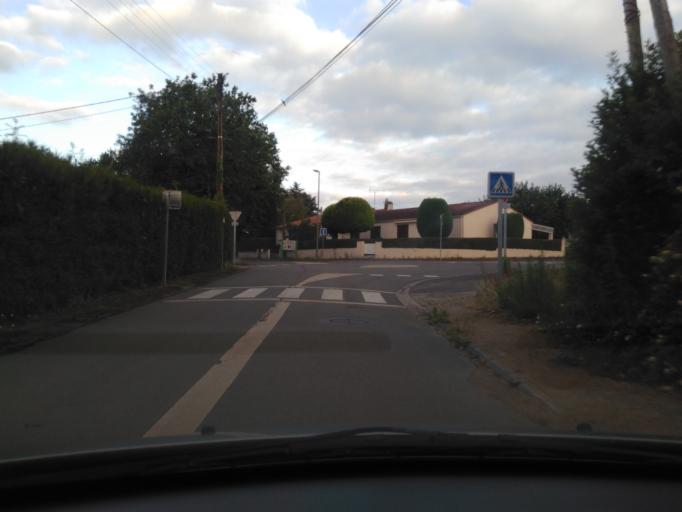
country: FR
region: Pays de la Loire
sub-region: Departement de la Vendee
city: Dompierre-sur-Yon
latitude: 46.7331
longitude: -1.3953
